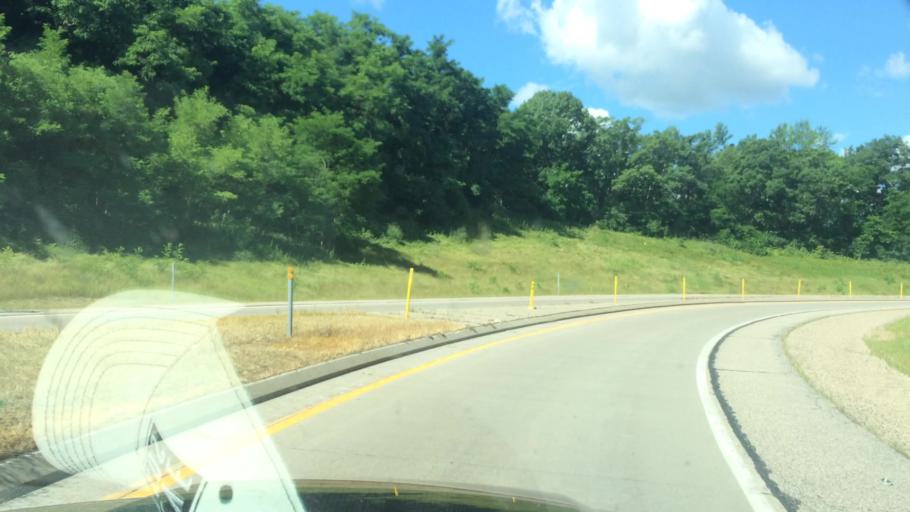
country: US
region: Wisconsin
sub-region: Waupaca County
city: Waupaca
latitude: 44.3363
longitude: -89.0678
